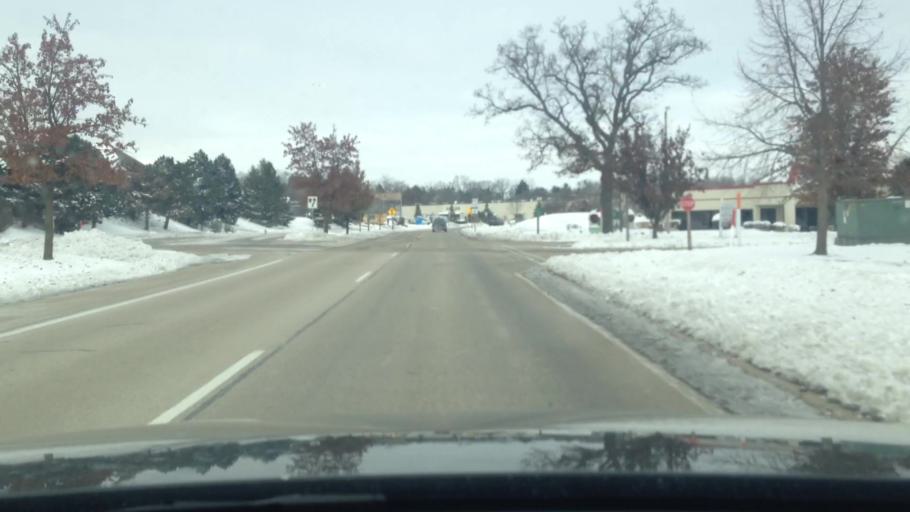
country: US
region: Wisconsin
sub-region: Walworth County
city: Lake Geneva
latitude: 42.5880
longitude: -88.4128
